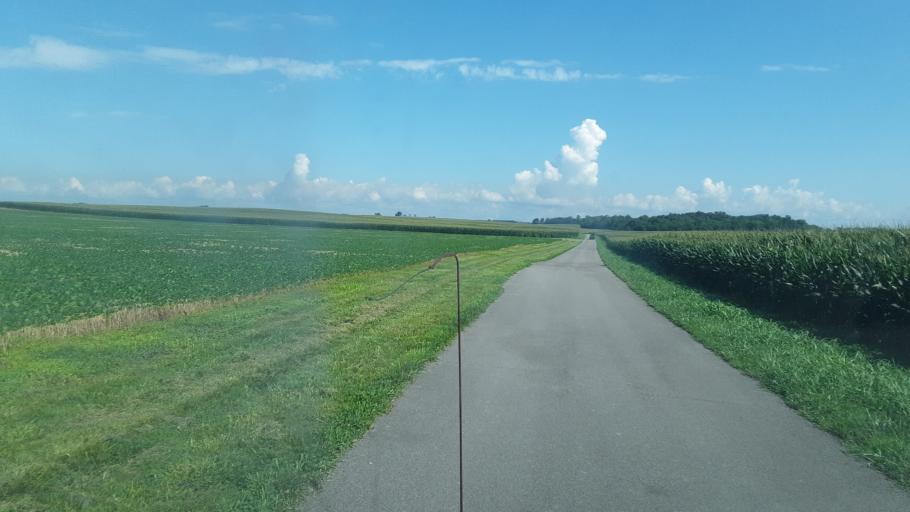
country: US
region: Kentucky
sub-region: Todd County
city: Elkton
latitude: 36.7605
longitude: -87.2281
